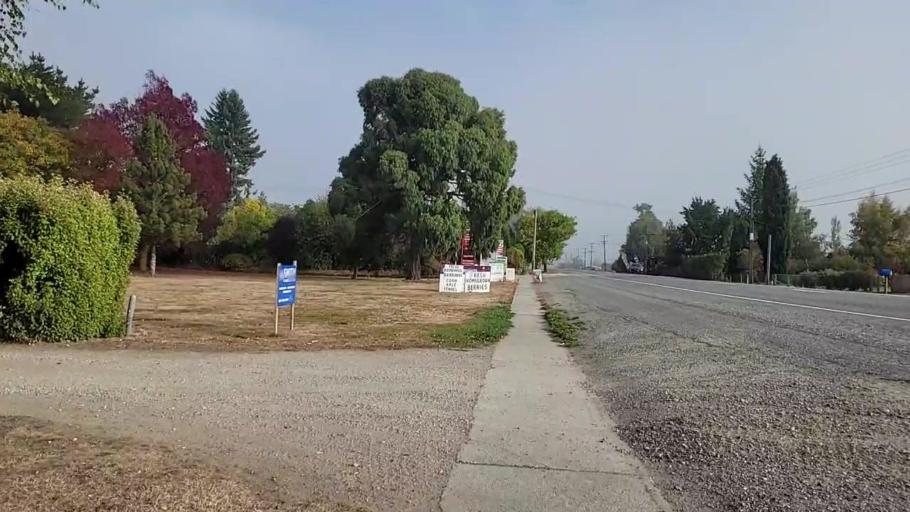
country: NZ
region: Southland
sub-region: Gore District
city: Gore
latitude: -45.6349
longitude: 169.3644
